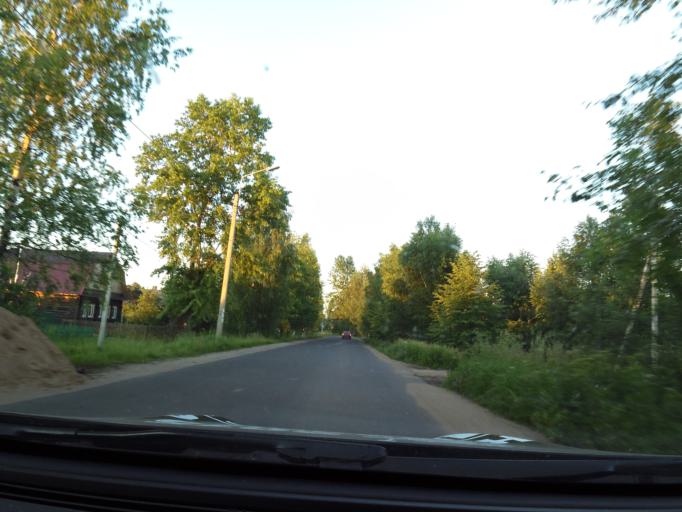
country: RU
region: Jaroslavl
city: Lyubim
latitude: 58.3568
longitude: 40.6705
